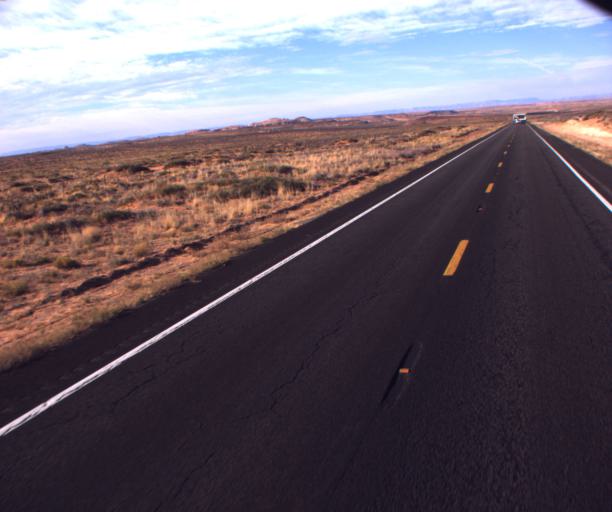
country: US
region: Arizona
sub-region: Apache County
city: Many Farms
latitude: 36.9408
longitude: -109.5455
